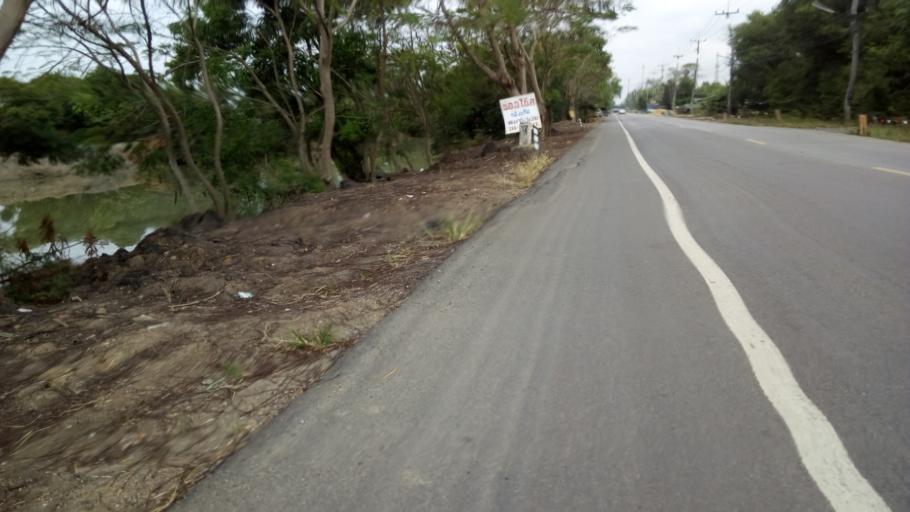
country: TH
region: Pathum Thani
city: Nong Suea
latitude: 14.2062
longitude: 100.8234
